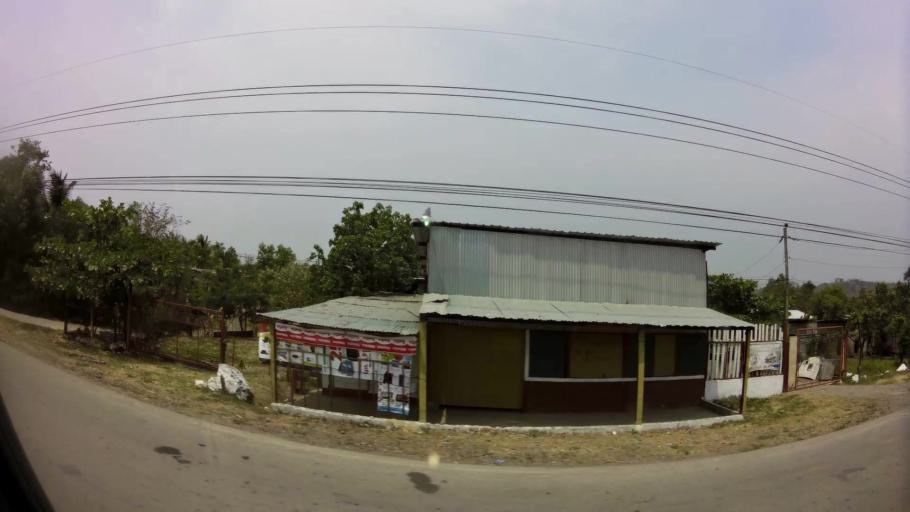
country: HN
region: Cortes
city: El Plan
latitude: 15.2976
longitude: -87.9808
